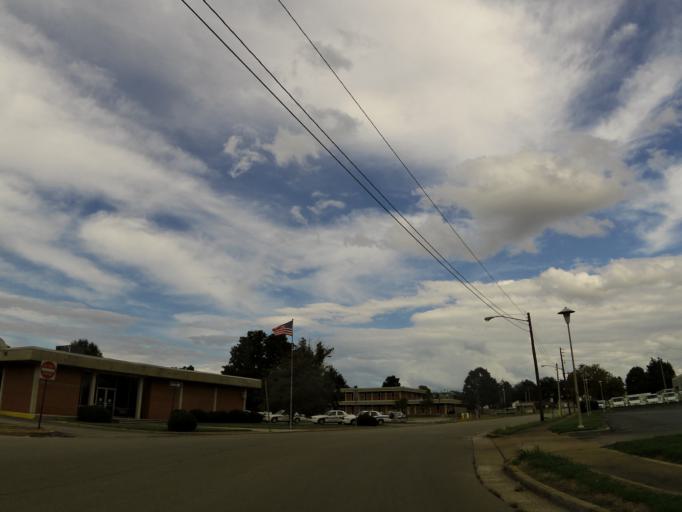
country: US
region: Kentucky
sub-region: Christian County
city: Hopkinsville
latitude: 36.8709
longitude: -87.4879
